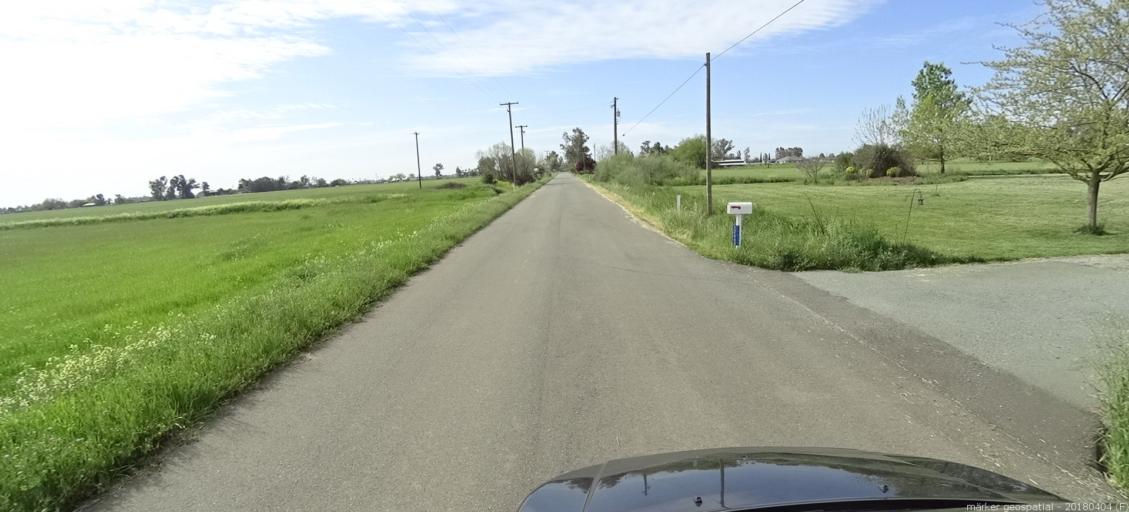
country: US
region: California
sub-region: Sacramento County
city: Herald
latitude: 38.2967
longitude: -121.2773
